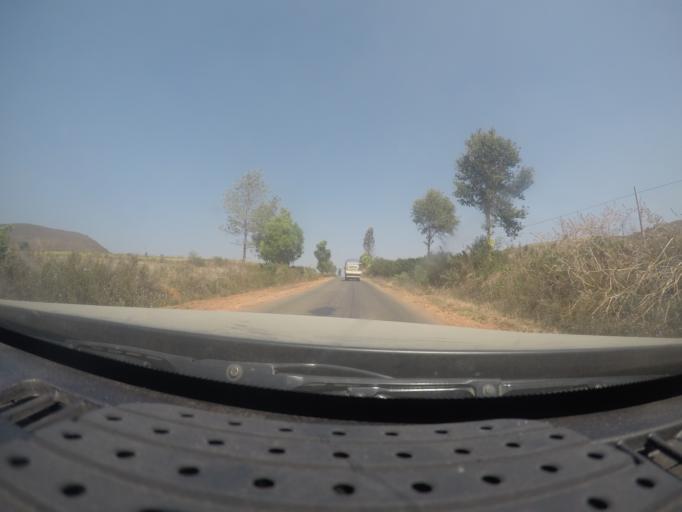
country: MM
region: Shan
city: Taunggyi
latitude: 20.8274
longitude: 96.6065
